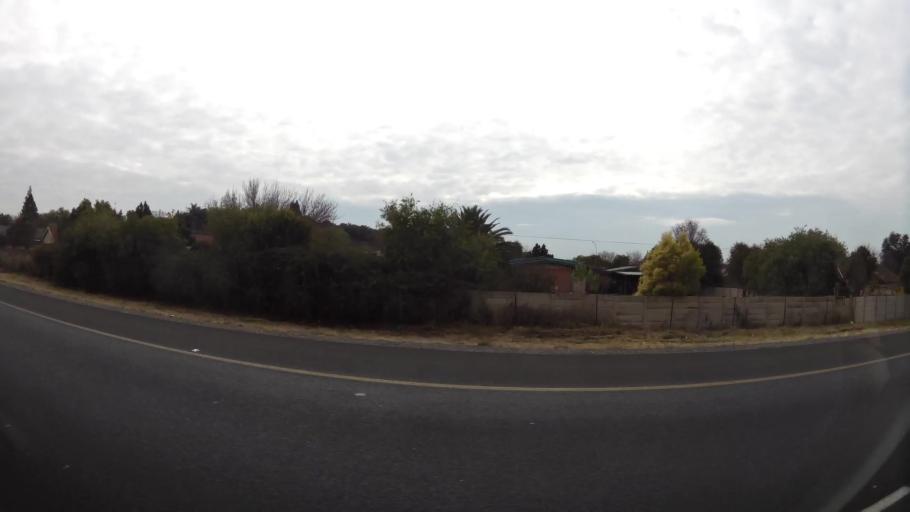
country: ZA
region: Orange Free State
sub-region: Mangaung Metropolitan Municipality
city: Bloemfontein
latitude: -29.1583
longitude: 26.1776
